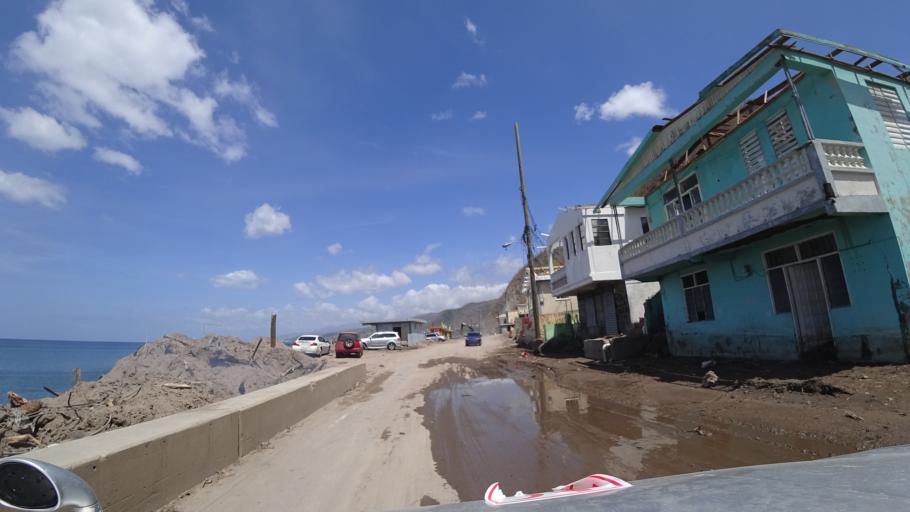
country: DM
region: Saint Luke
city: Pointe Michel
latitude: 15.2632
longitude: -61.3773
